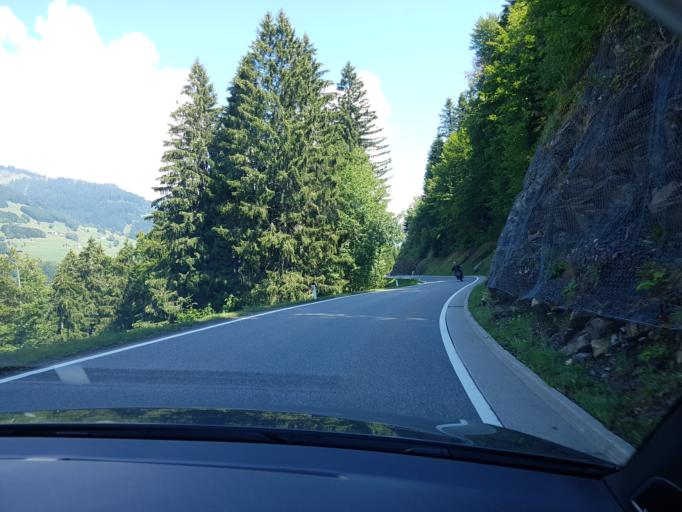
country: AT
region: Vorarlberg
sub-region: Politischer Bezirk Bludenz
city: Ludesch
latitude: 47.2063
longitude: 9.7963
